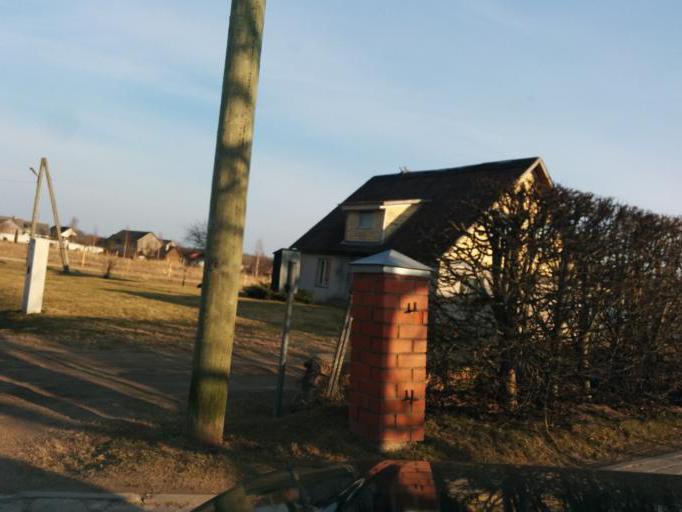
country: LV
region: Lecava
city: Iecava
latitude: 56.6621
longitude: 24.2375
